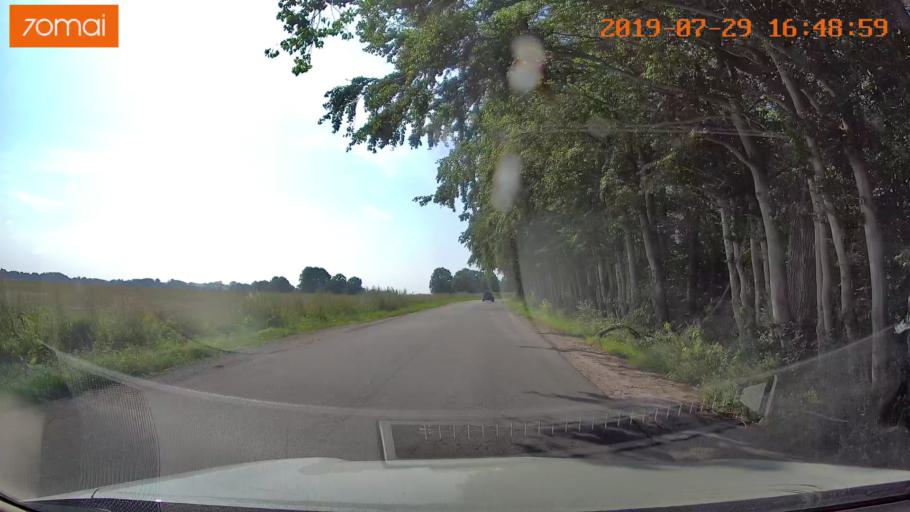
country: RU
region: Kaliningrad
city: Primorsk
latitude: 54.7910
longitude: 20.0701
